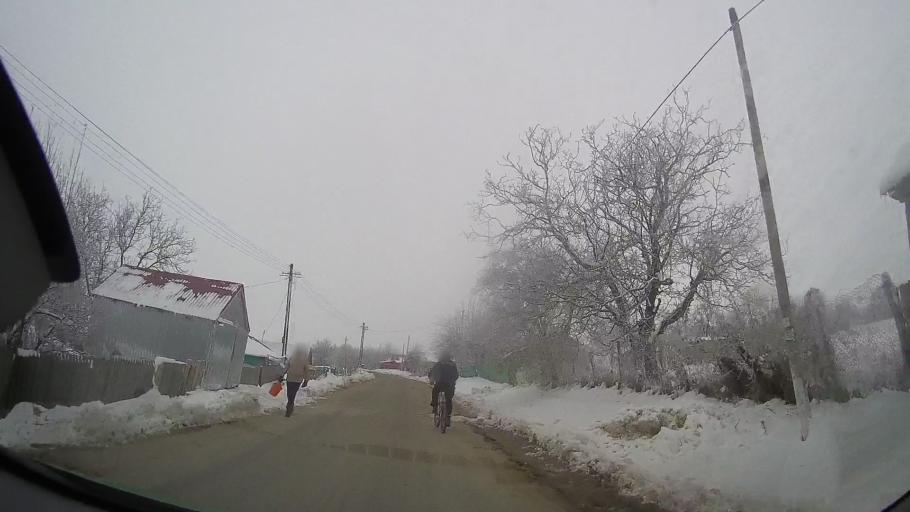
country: RO
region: Neamt
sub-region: Comuna Pancesti
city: Pancesti
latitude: 46.9090
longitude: 27.1579
